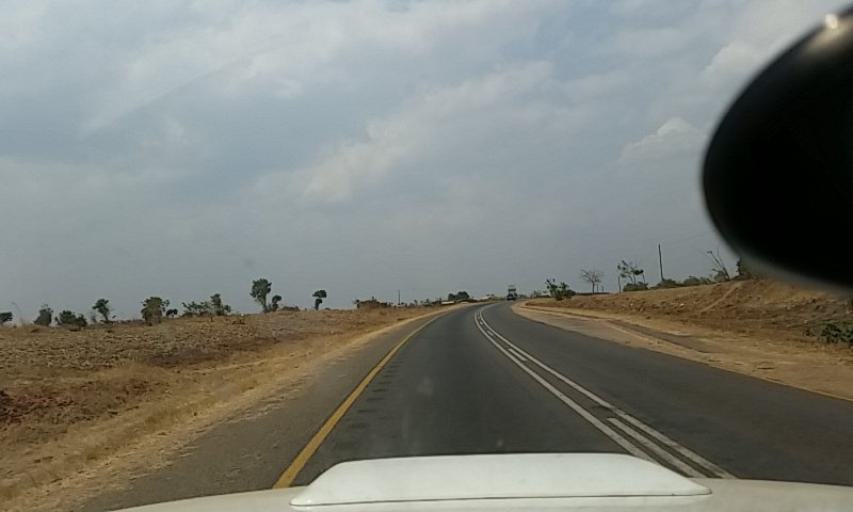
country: MW
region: Central Region
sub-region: Lilongwe District
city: Lilongwe
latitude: -13.8273
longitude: 33.8552
